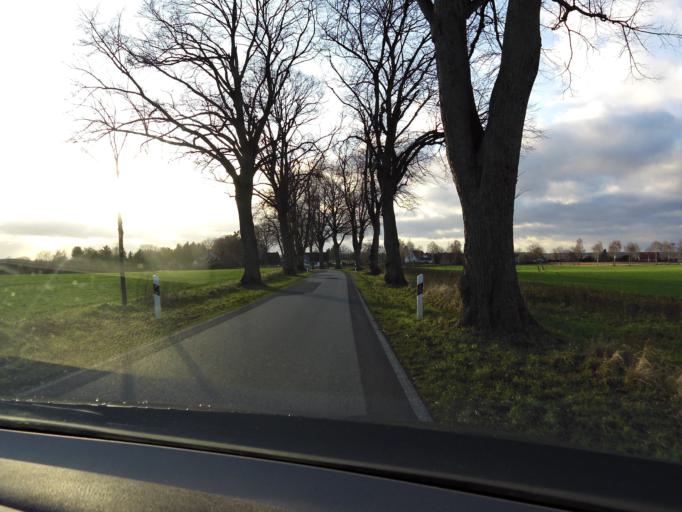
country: DE
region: Schleswig-Holstein
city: Kittlitz
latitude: 53.6657
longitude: 10.9215
